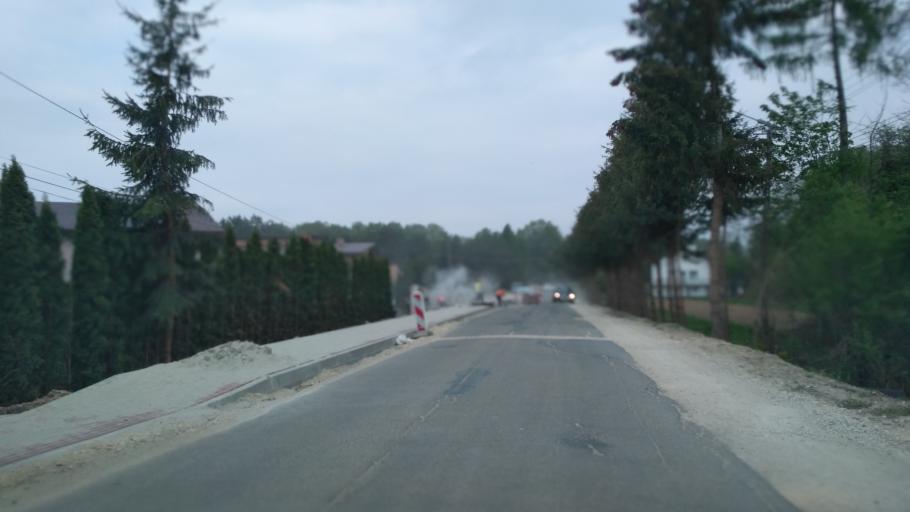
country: PL
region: Lesser Poland Voivodeship
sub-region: Powiat tarnowski
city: Skrzyszow
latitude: 49.9828
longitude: 21.0636
